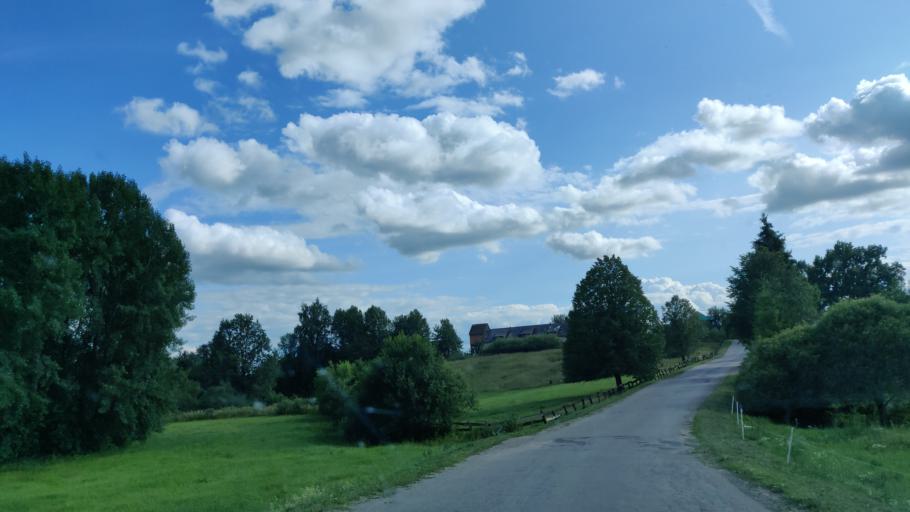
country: LT
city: Varniai
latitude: 55.5952
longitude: 22.3105
